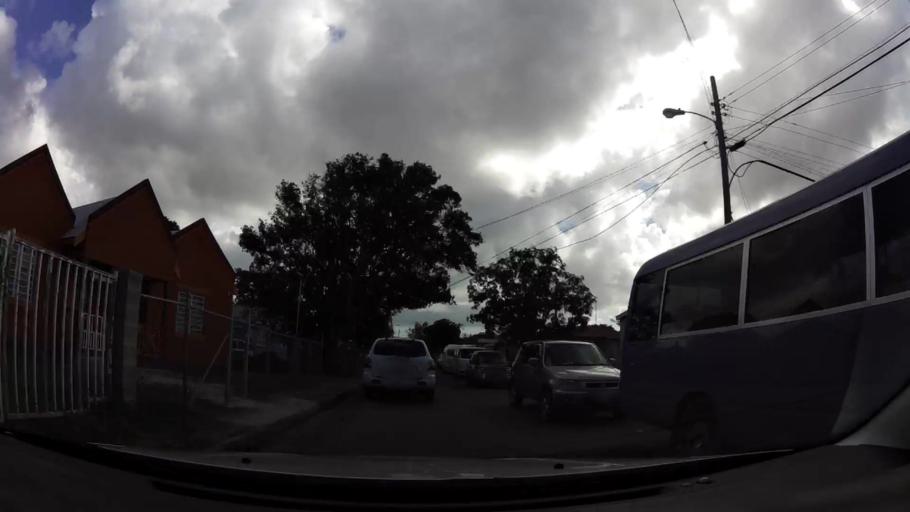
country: AG
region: Saint John
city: Saint John's
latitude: 17.1062
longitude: -61.8419
